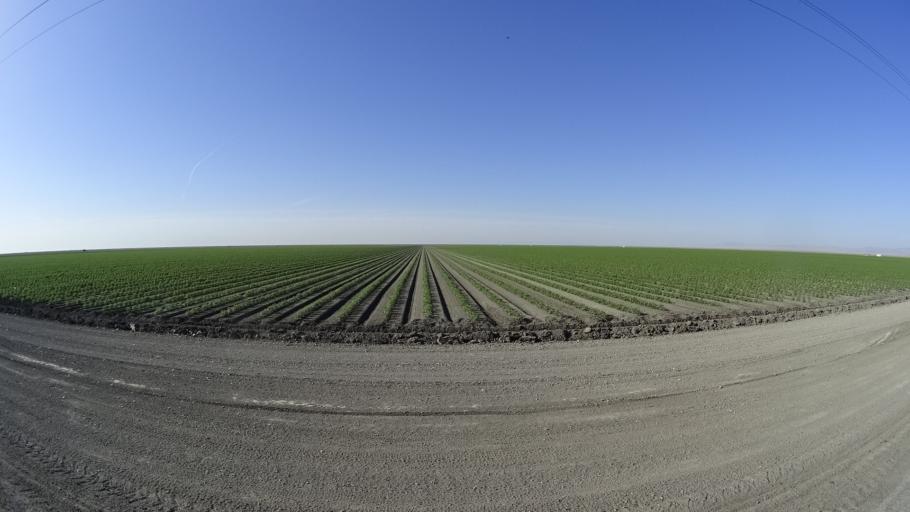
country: US
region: California
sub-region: Kings County
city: Stratford
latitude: 36.0797
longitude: -119.7740
